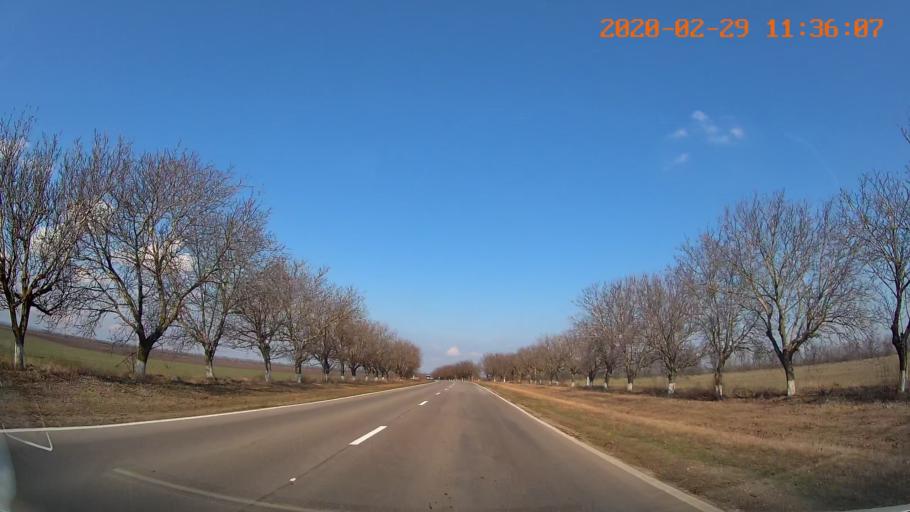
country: MD
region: Rezina
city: Saharna
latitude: 47.5910
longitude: 29.0588
